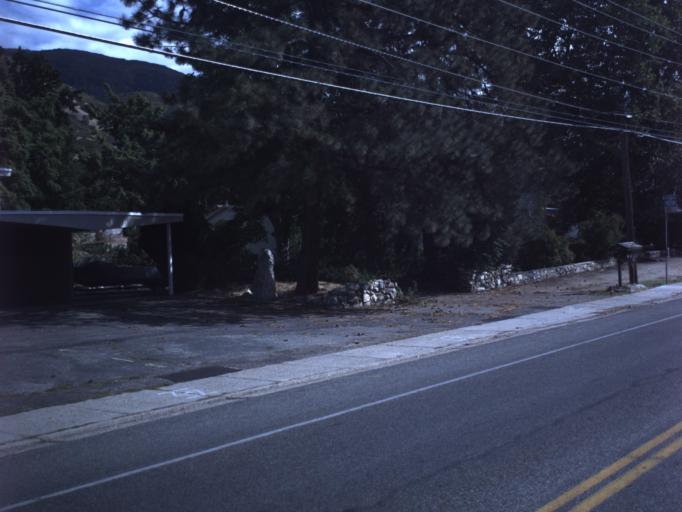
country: US
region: Utah
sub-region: Davis County
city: Farmington
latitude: 40.9778
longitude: -111.8833
